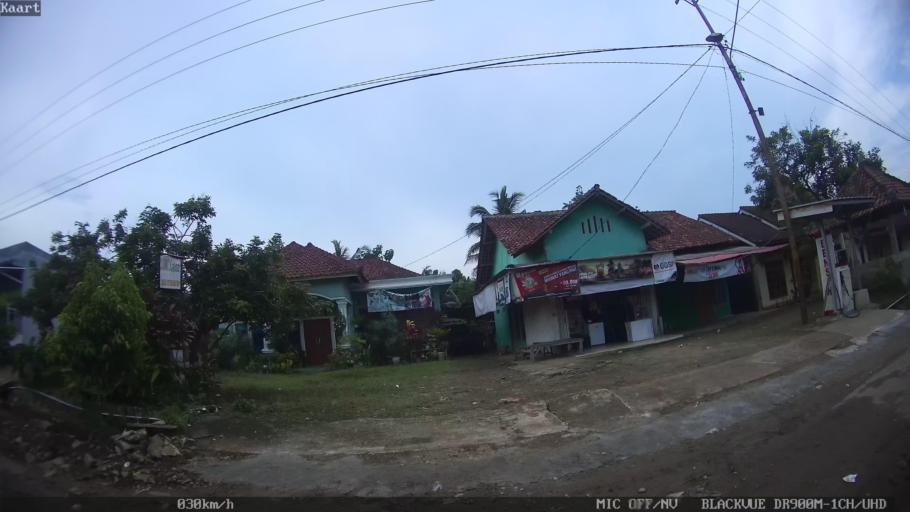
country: ID
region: Lampung
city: Bandarlampung
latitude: -5.4354
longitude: 105.2306
